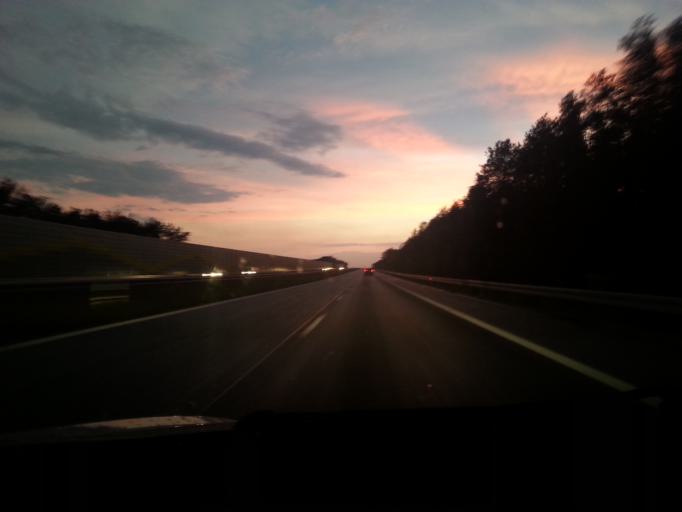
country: PL
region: Lodz Voivodeship
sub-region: Powiat zdunskowolski
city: Zdunska Wola
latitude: 51.5693
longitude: 18.9702
